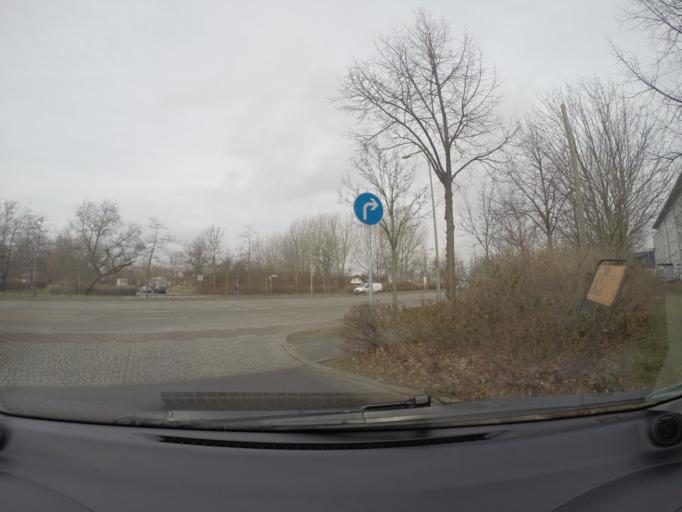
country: DE
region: Berlin
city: Marzahn
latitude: 52.5435
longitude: 13.5711
